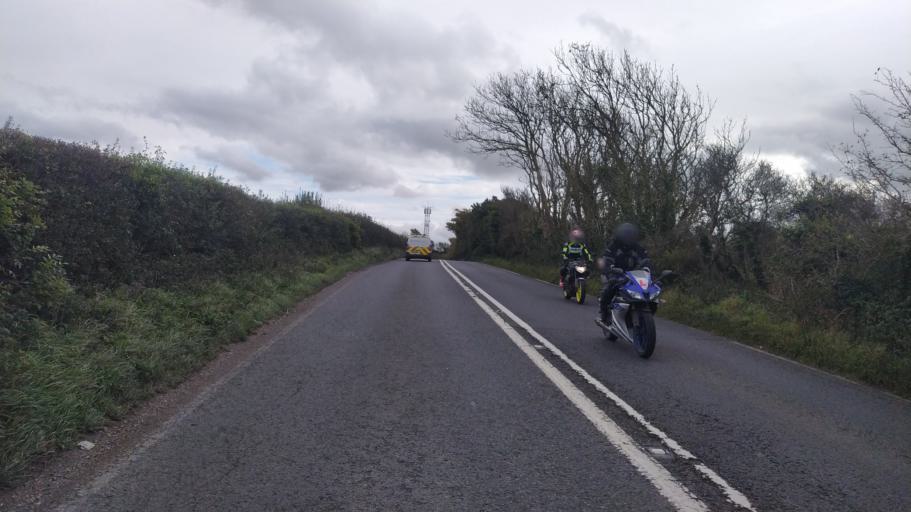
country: GB
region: England
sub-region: Dorset
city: Dorchester
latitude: 50.7142
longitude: -2.5179
